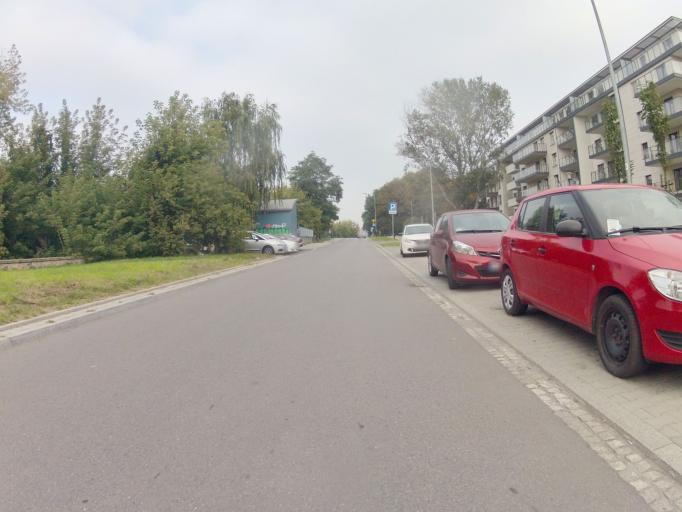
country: PL
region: Lesser Poland Voivodeship
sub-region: Krakow
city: Krakow
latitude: 50.0430
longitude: 19.9399
